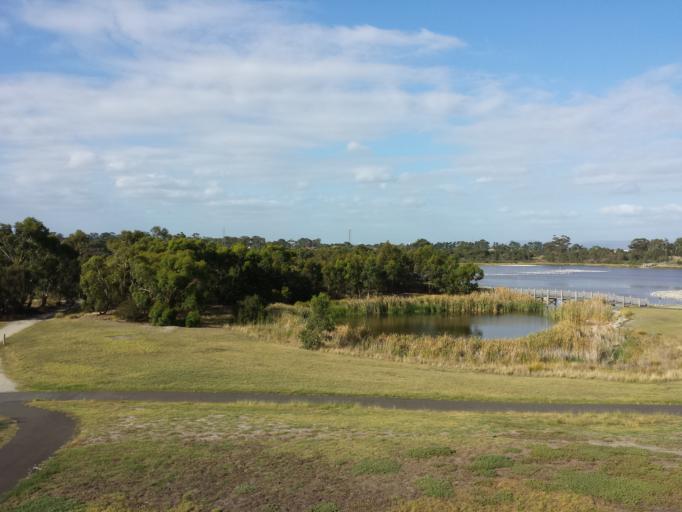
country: AU
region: Victoria
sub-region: Monash
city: Oakleigh South
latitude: -37.9431
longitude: 145.0809
